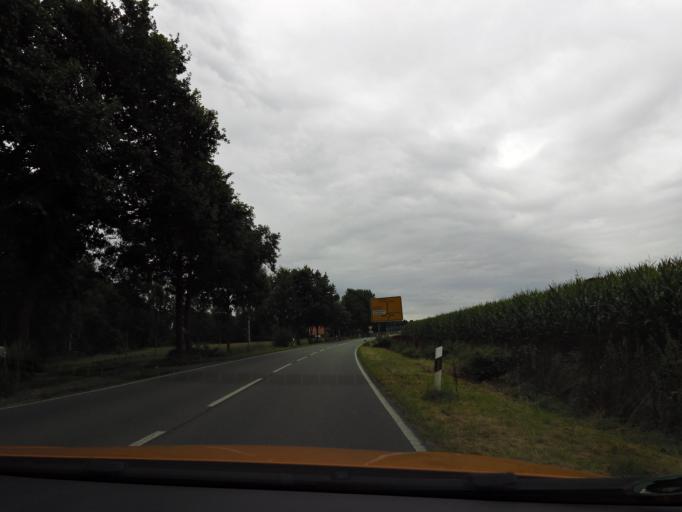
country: DE
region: Lower Saxony
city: Bad Zwischenahn
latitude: 53.2349
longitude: 7.9916
